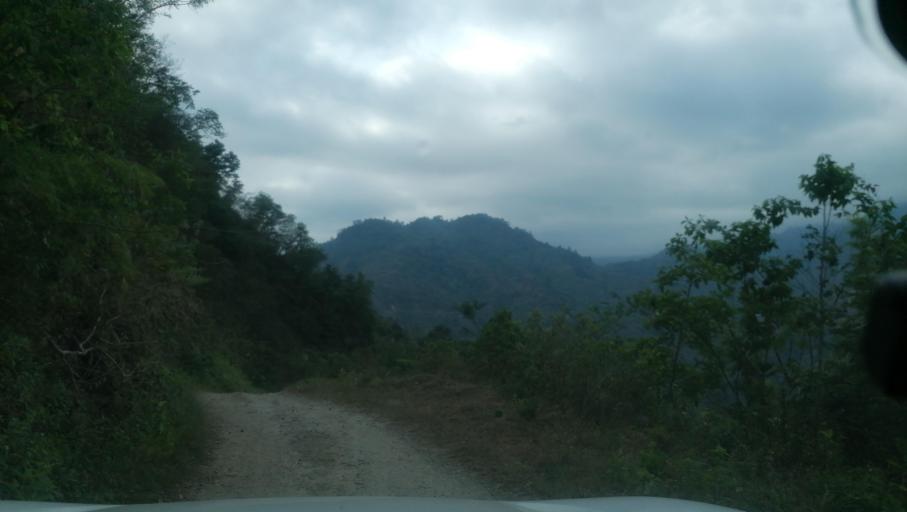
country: MX
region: Chiapas
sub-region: Cacahoatan
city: Benito Juarez
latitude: 15.1650
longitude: -92.1713
